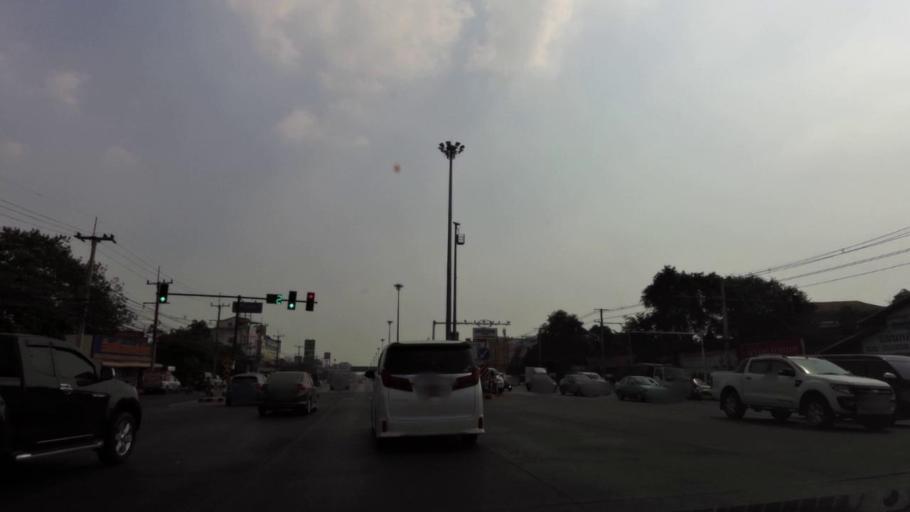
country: TH
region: Phra Nakhon Si Ayutthaya
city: Phra Nakhon Si Ayutthaya
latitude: 14.3532
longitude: 100.6002
